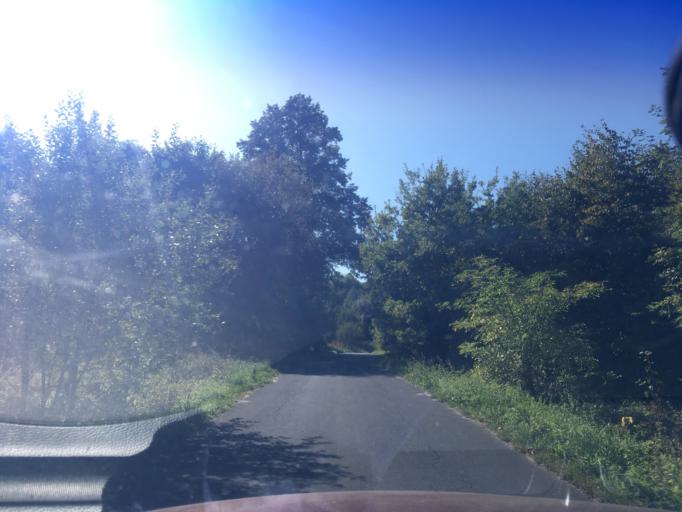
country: PL
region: Lower Silesian Voivodeship
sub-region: Powiat lubanski
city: Swieradow-Zdroj
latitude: 50.9456
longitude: 15.3095
